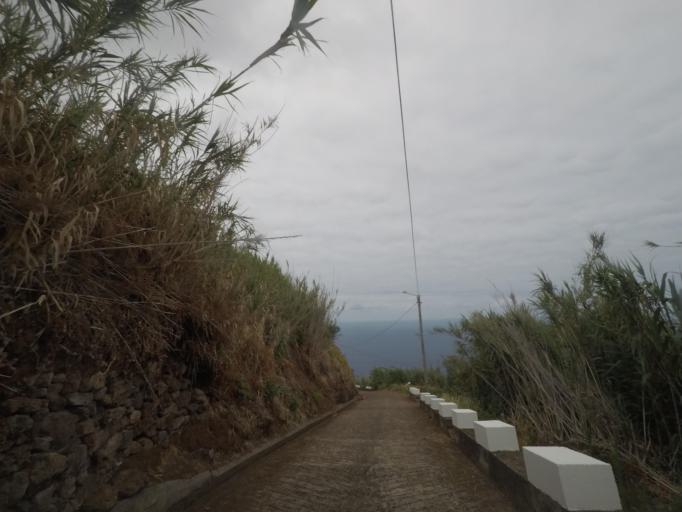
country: PT
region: Madeira
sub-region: Porto Moniz
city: Porto Moniz
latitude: 32.8635
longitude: -17.1798
